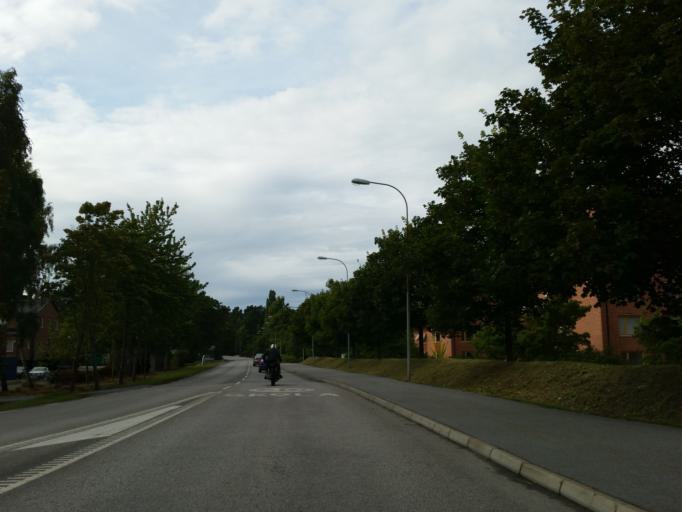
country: SE
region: Stockholm
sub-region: Sollentuna Kommun
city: Sollentuna
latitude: 59.4481
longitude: 17.9401
